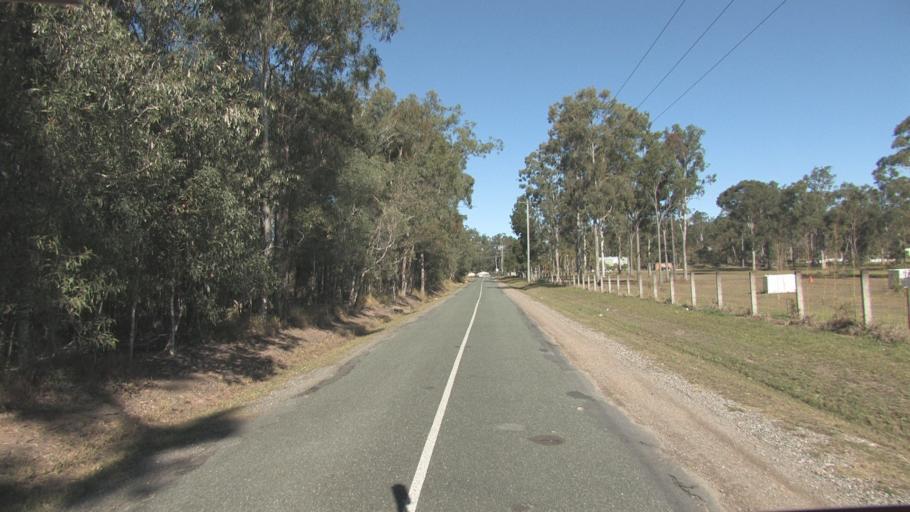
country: AU
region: Queensland
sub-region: Logan
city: Chambers Flat
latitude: -27.8018
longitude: 153.0711
